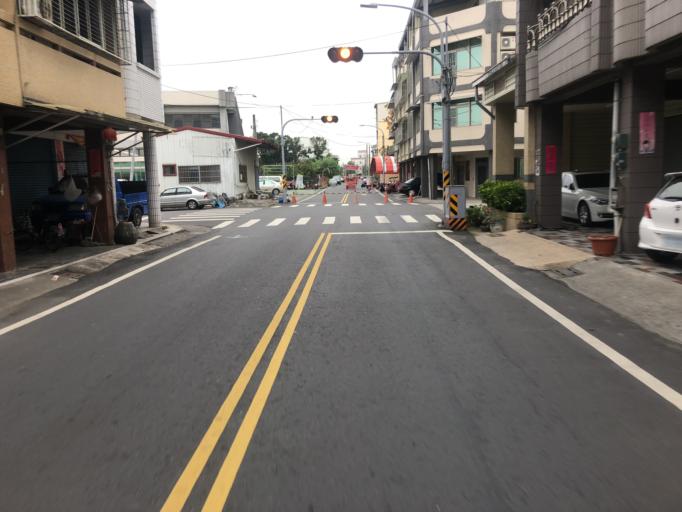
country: TW
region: Taiwan
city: Xinying
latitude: 23.1815
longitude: 120.2442
